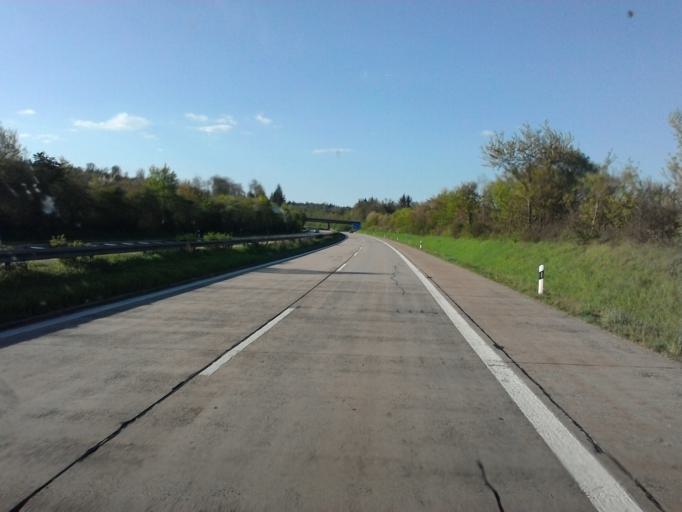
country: DE
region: Bavaria
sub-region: Regierungsbezirk Mittelfranken
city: Schillingsfurst
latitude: 49.2657
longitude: 10.2356
